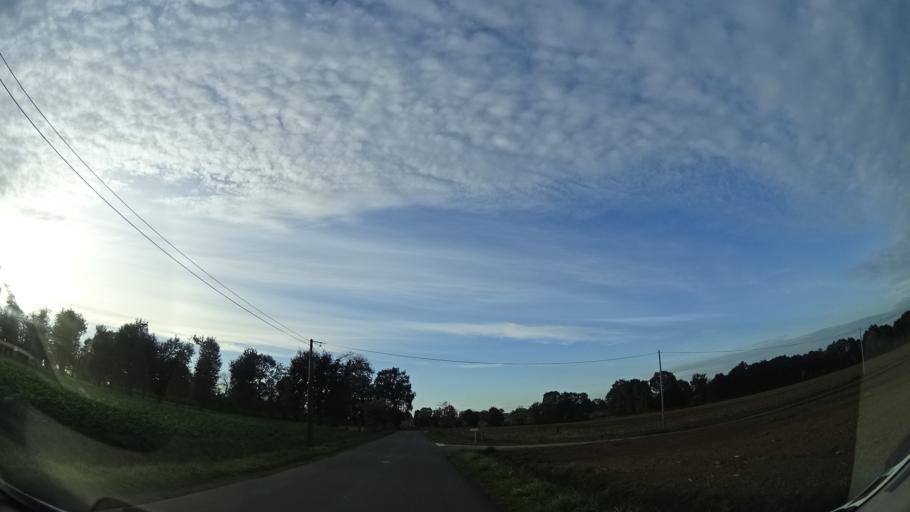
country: FR
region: Brittany
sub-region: Departement d'Ille-et-Vilaine
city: Geveze
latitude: 48.1887
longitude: -1.8059
